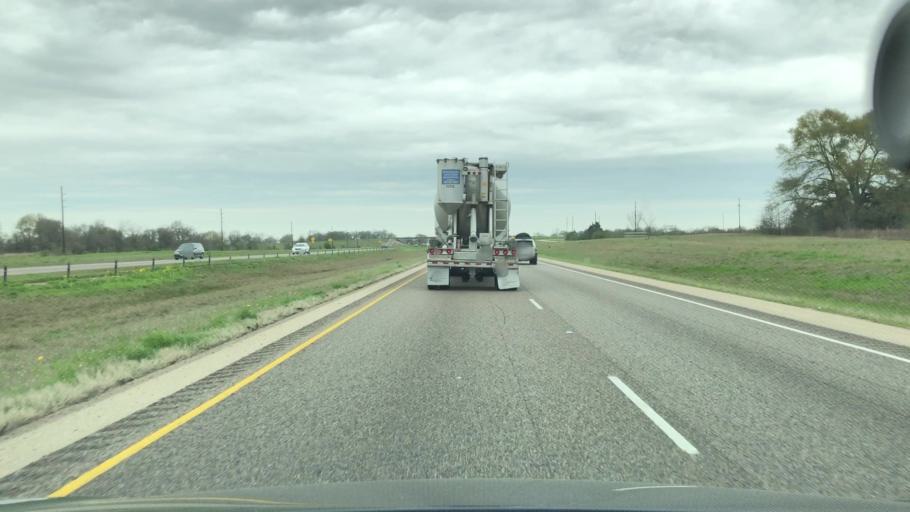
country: US
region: Texas
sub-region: Madison County
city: Madisonville
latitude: 31.0650
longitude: -95.9517
